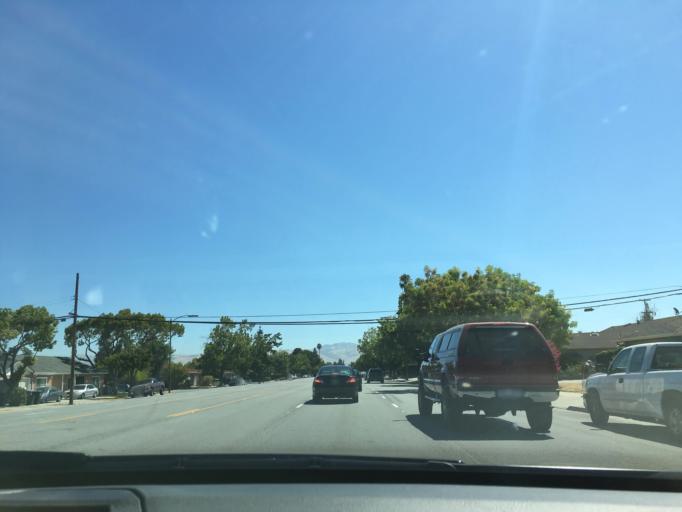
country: US
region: California
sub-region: Santa Clara County
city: Cambrian Park
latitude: 37.2683
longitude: -121.9032
